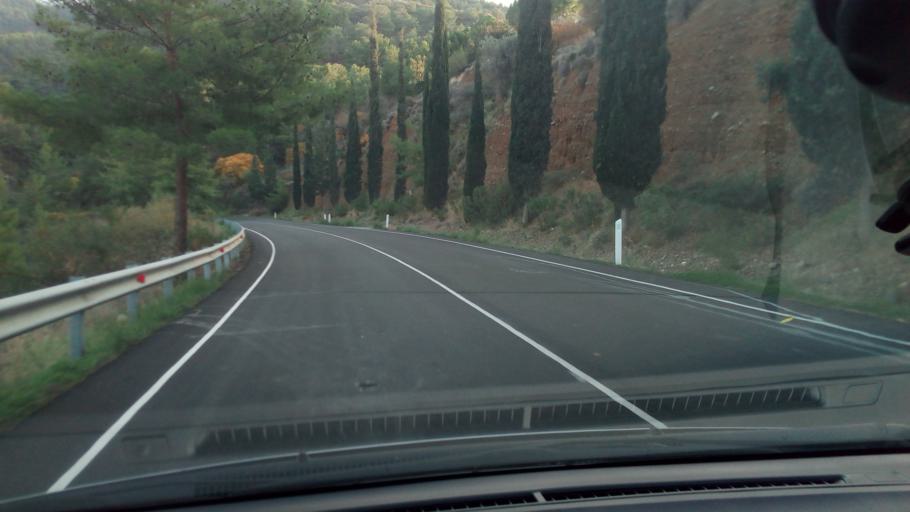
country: CY
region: Pafos
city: Polis
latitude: 35.1464
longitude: 32.5314
